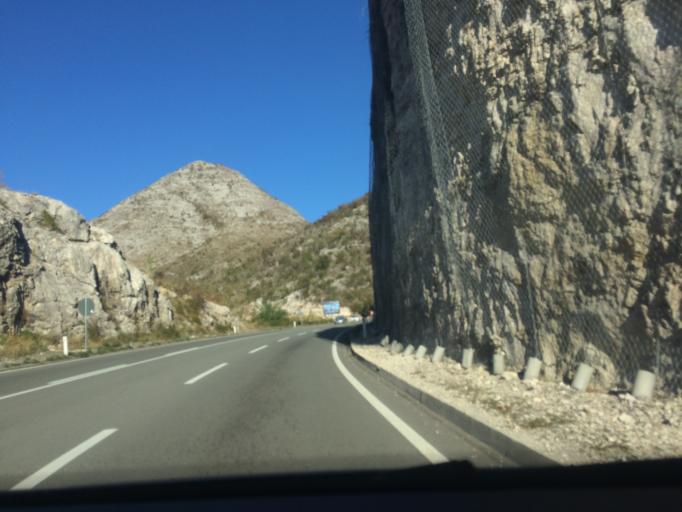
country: ME
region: Cetinje
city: Cetinje
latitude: 42.3813
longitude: 18.9688
